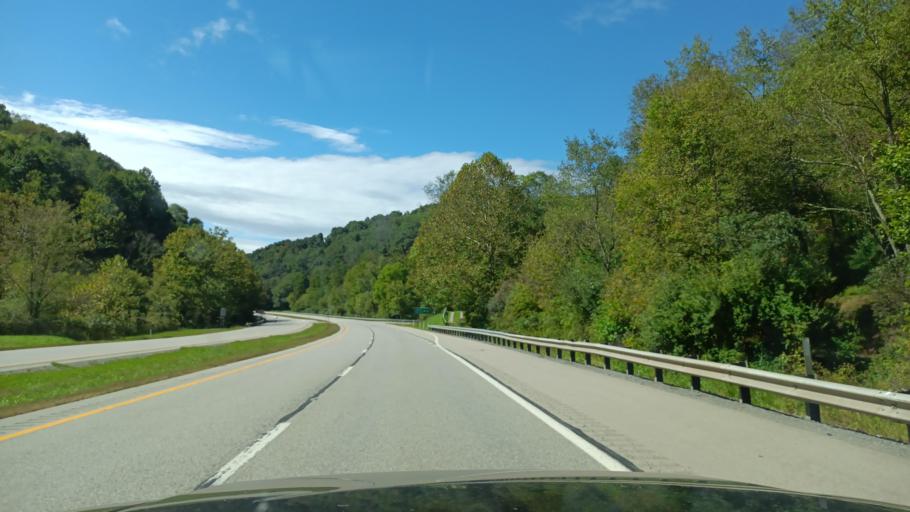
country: US
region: West Virginia
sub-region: Harrison County
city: Salem
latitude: 39.2854
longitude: -80.6533
